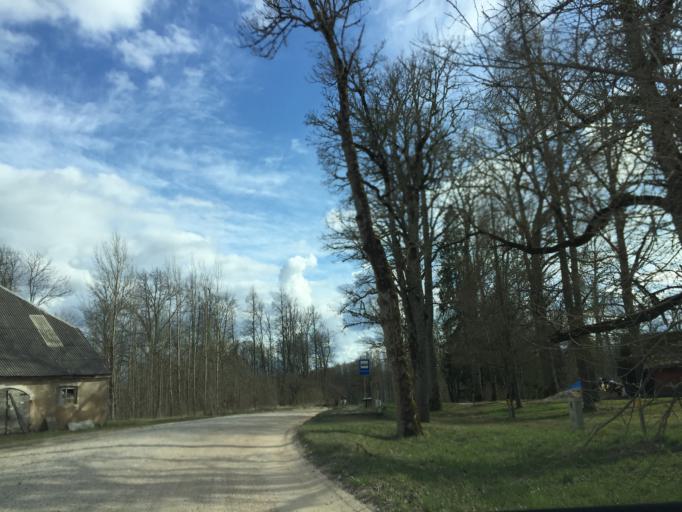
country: LV
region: Burtnieki
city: Matisi
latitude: 57.6141
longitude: 25.0796
